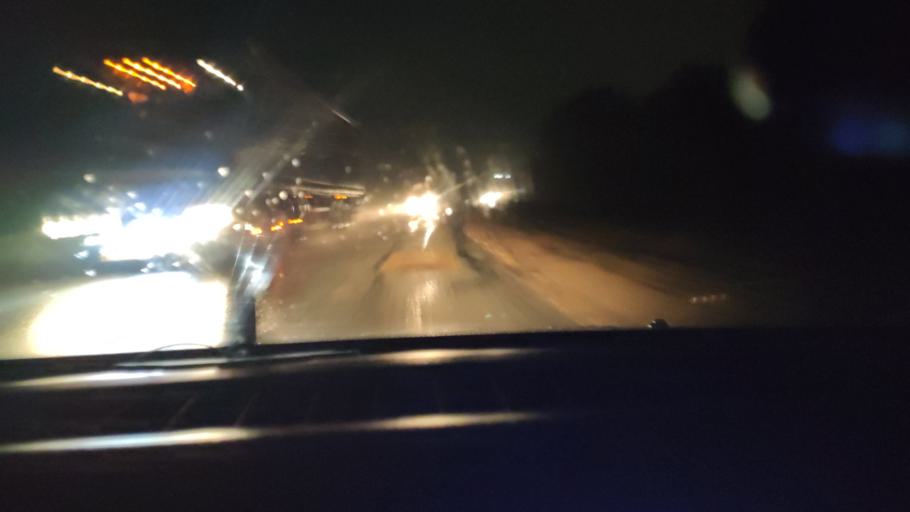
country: RU
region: Udmurtiya
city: Votkinsk
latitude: 57.0699
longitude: 54.0373
